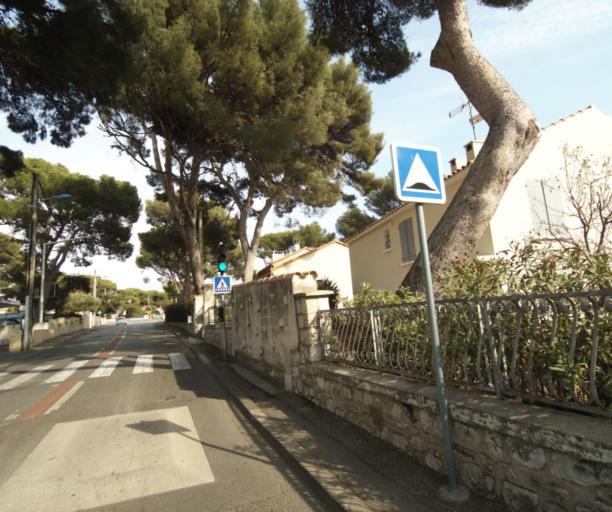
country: FR
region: Provence-Alpes-Cote d'Azur
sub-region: Departement des Bouches-du-Rhone
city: Sausset-les-Pins
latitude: 43.3310
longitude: 5.1176
